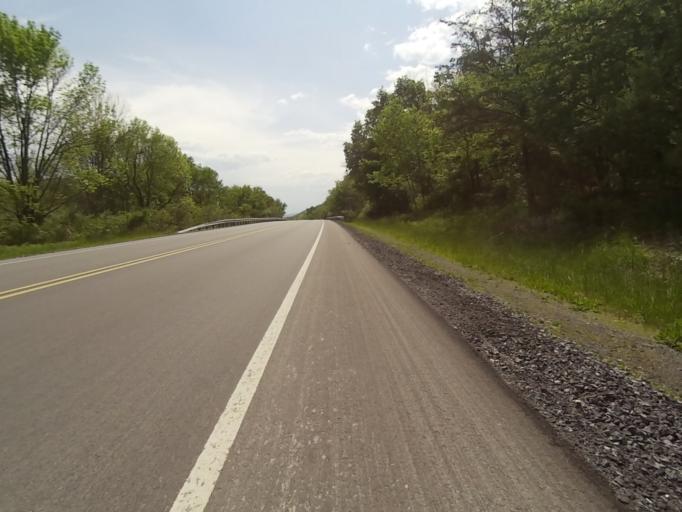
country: US
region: Pennsylvania
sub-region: Centre County
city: Zion
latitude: 41.0329
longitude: -77.6572
